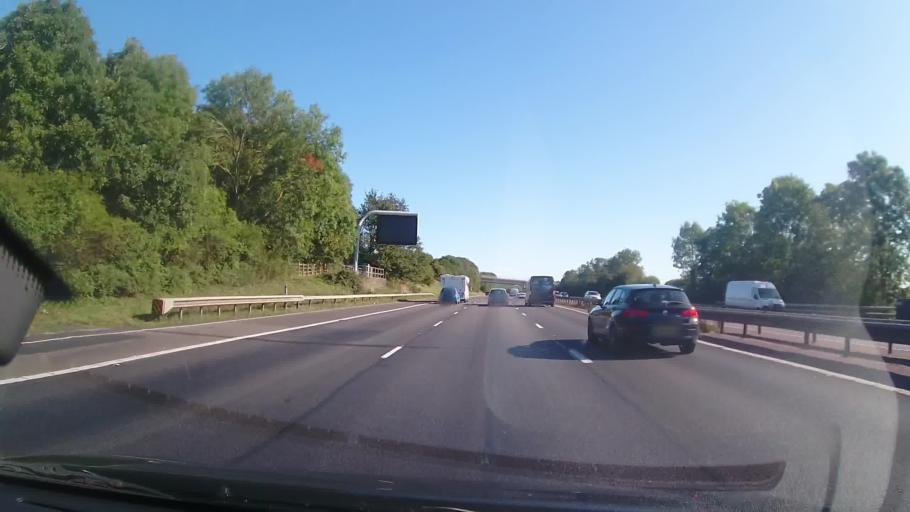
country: GB
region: England
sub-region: Oxfordshire
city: Adderbury
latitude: 52.0101
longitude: -1.2771
